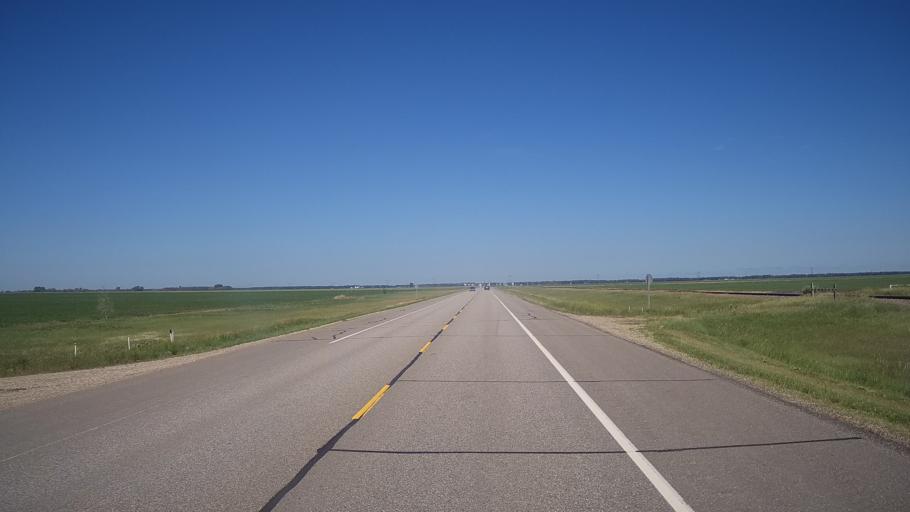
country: CA
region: Manitoba
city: Portage la Prairie
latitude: 50.1034
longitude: -98.5376
